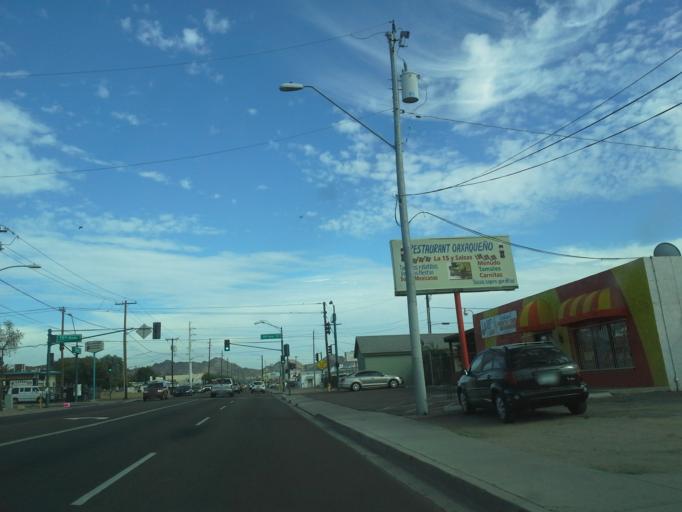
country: US
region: Arizona
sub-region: Maricopa County
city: Glendale
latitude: 33.5712
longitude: -112.0921
